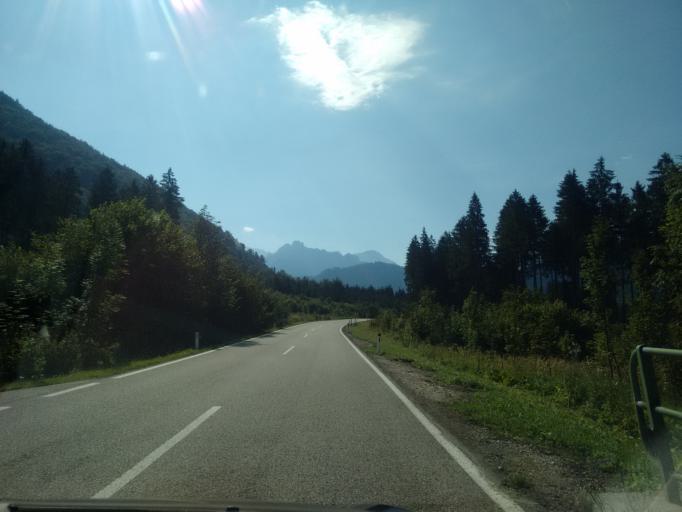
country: AT
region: Upper Austria
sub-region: Politischer Bezirk Gmunden
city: Gruenau im Almtal
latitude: 47.8022
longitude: 13.9526
